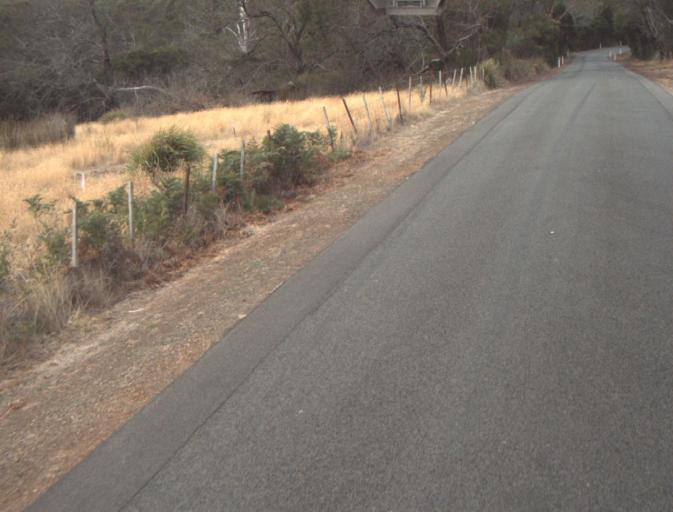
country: AU
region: Tasmania
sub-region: Launceston
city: Mayfield
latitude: -41.2831
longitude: 147.0265
